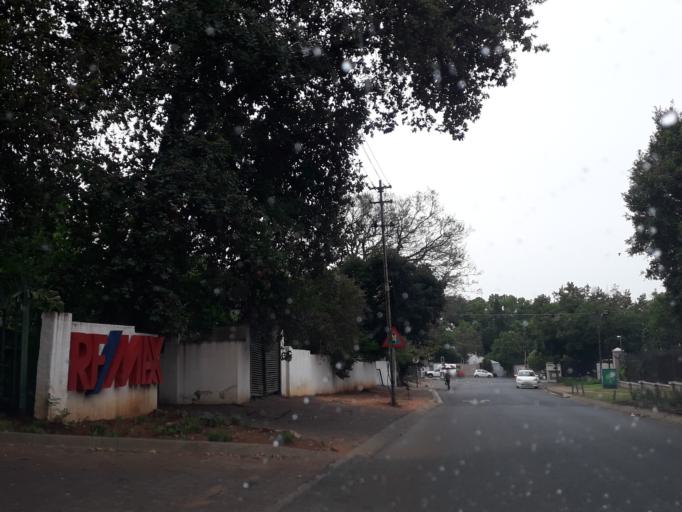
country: ZA
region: Gauteng
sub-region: City of Johannesburg Metropolitan Municipality
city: Johannesburg
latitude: -26.1158
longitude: 28.0501
